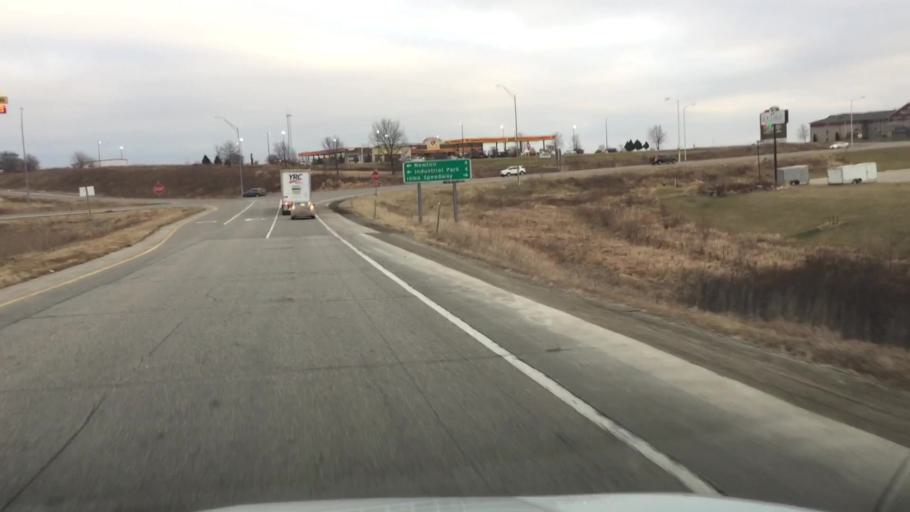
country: US
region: Iowa
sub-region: Jasper County
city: Newton
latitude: 41.6816
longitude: -93.0015
